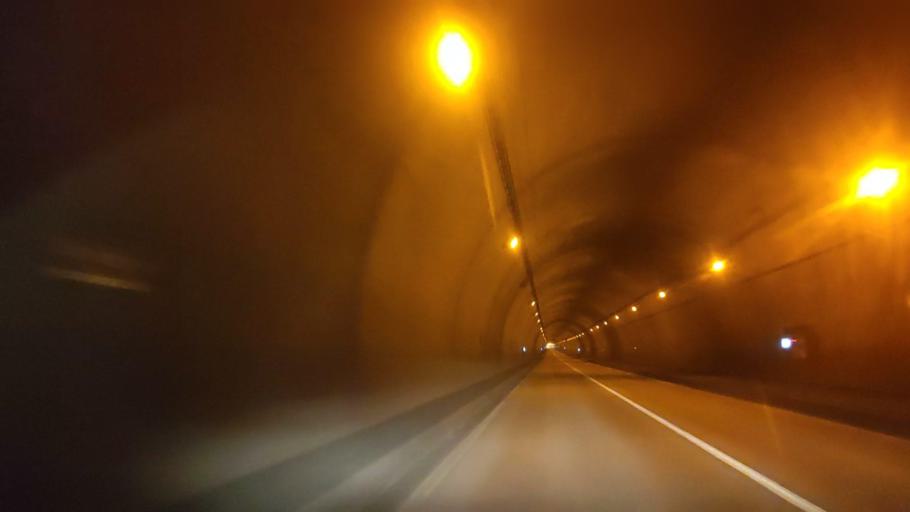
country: JP
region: Hokkaido
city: Date
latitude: 42.5582
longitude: 140.7602
